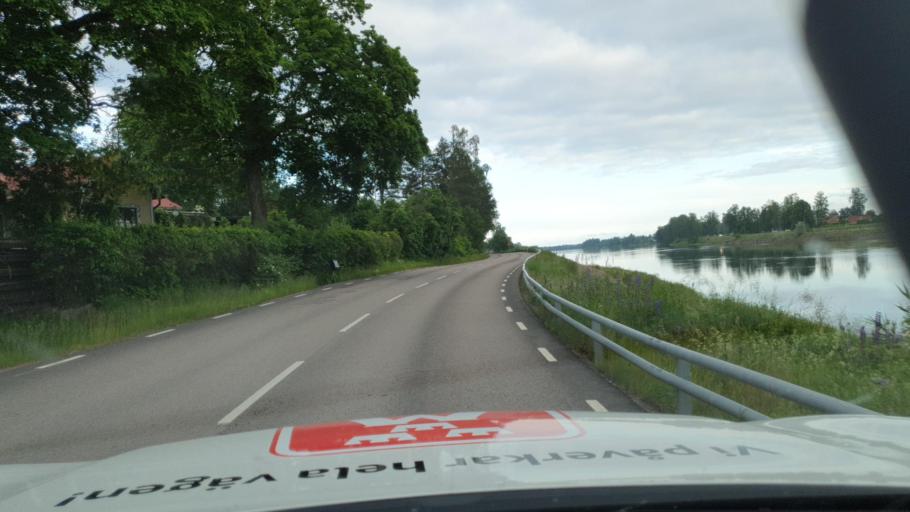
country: SE
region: Vaermland
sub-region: Karlstads Kommun
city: Karlstad
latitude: 59.4229
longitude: 13.4813
